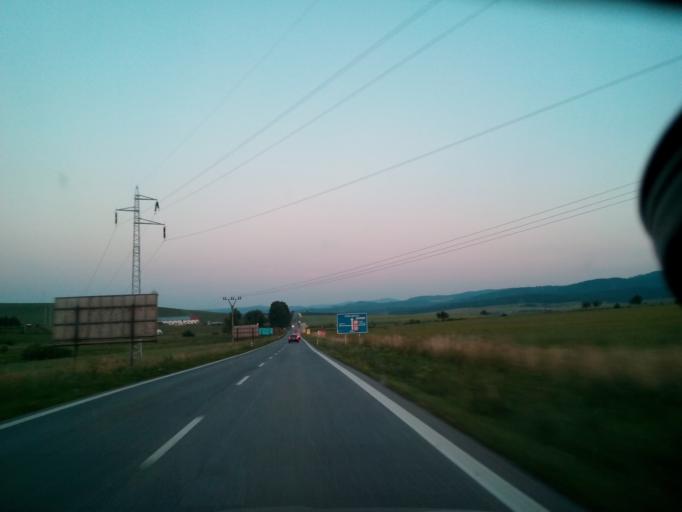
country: SK
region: Kosicky
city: Spisska Nova Ves
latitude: 48.9779
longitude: 20.4868
